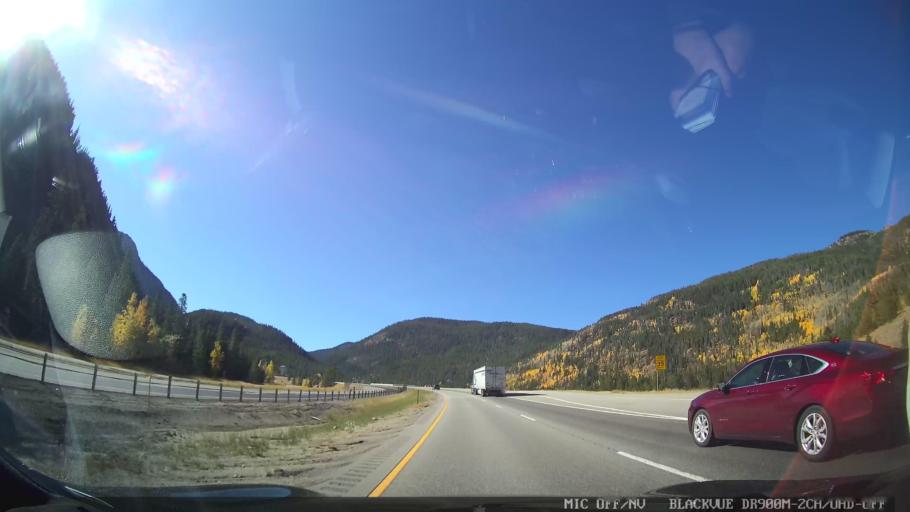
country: US
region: Colorado
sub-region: Summit County
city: Frisco
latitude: 39.5410
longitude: -106.1416
